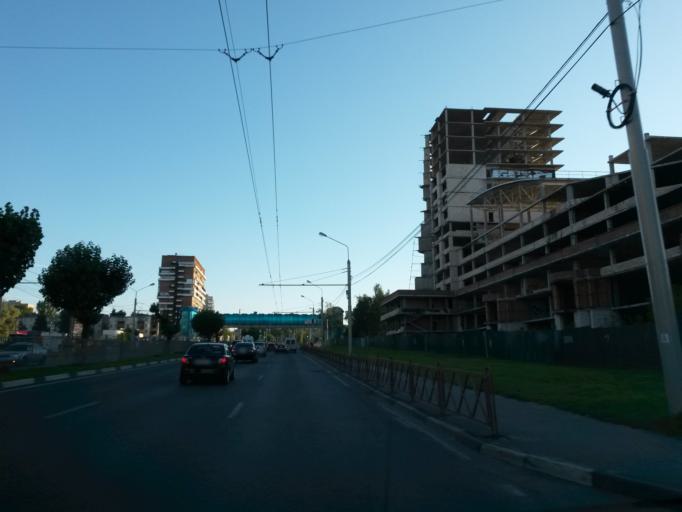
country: RU
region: Jaroslavl
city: Yaroslavl
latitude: 57.5945
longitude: 39.8660
